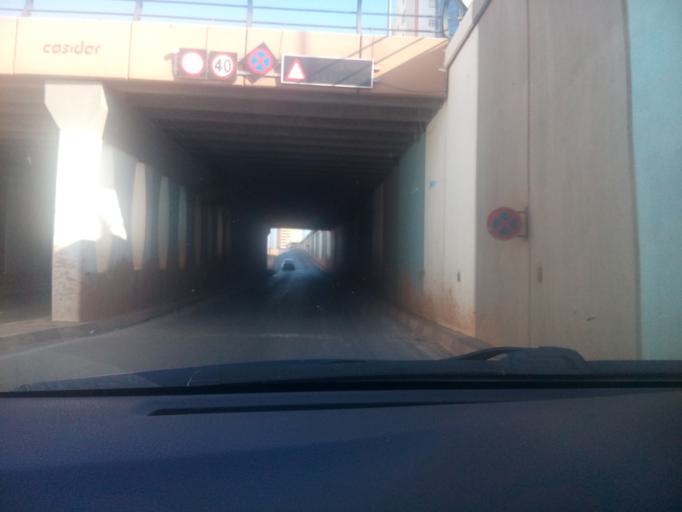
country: DZ
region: Oran
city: Oran
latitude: 35.6754
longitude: -0.6777
